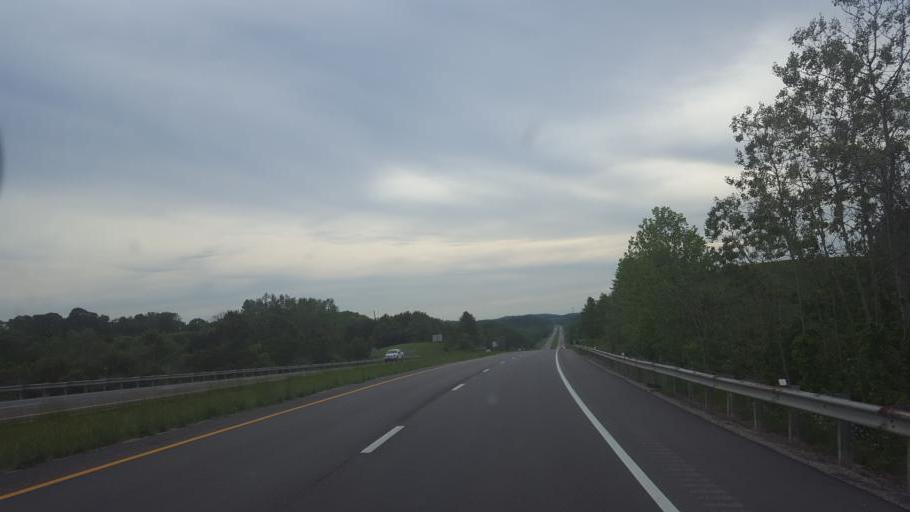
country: US
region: Ohio
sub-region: Vinton County
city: McArthur
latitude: 39.1716
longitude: -82.2969
